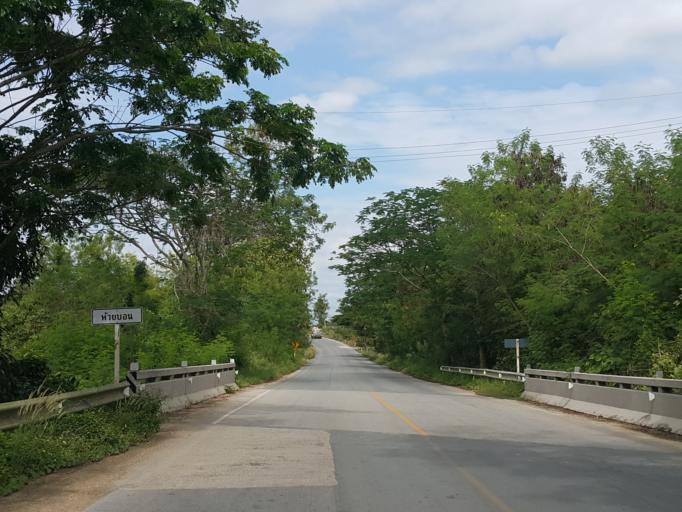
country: TH
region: Lampang
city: Lampang
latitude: 18.4072
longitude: 99.4531
